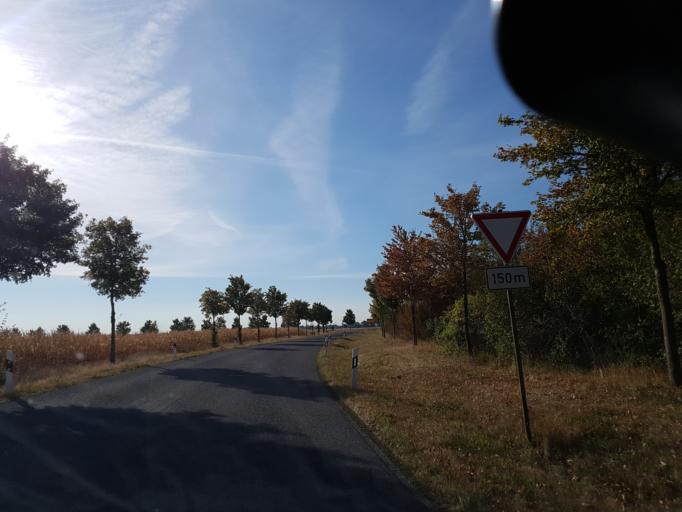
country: DE
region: Saxony
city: Nauwalde
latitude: 51.4387
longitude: 13.3553
